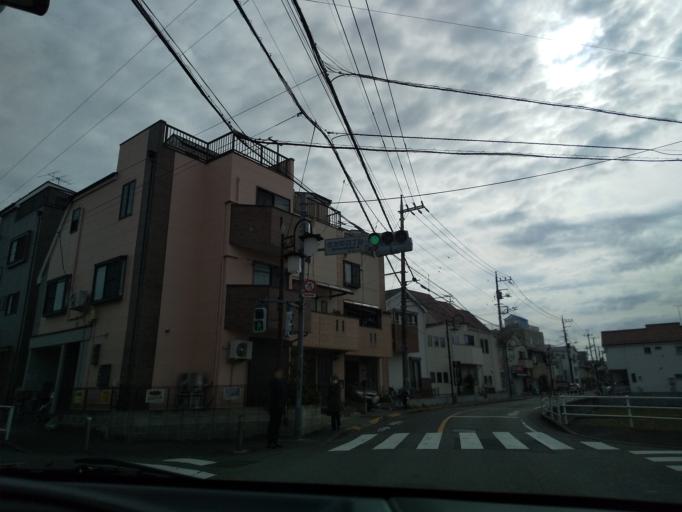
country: JP
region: Tokyo
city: Kokubunji
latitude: 35.6617
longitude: 139.4518
